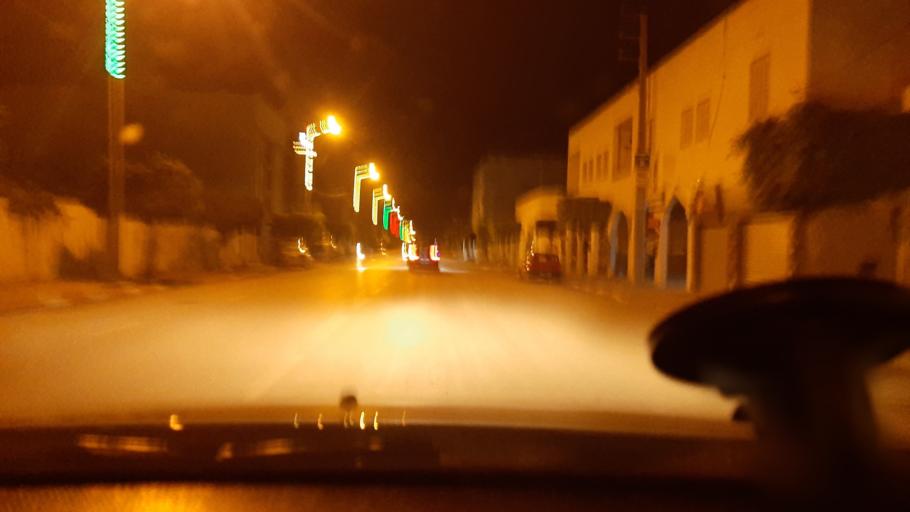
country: TN
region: Safaqis
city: Sfax
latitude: 34.7778
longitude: 10.7264
